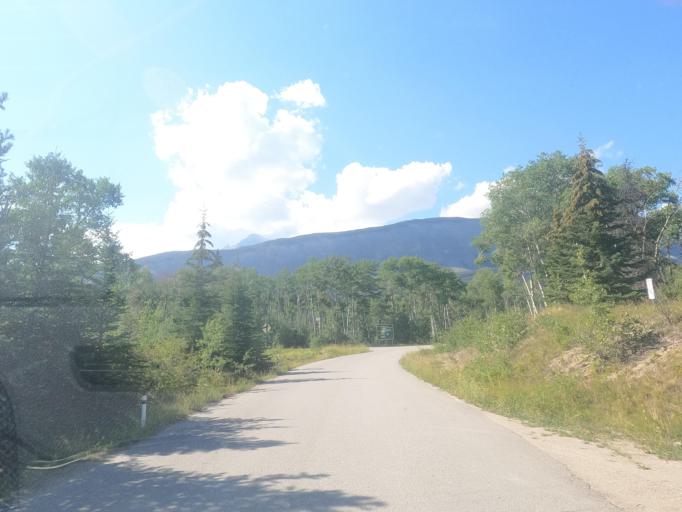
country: CA
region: Alberta
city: Jasper Park Lodge
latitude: 52.9710
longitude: -118.0589
